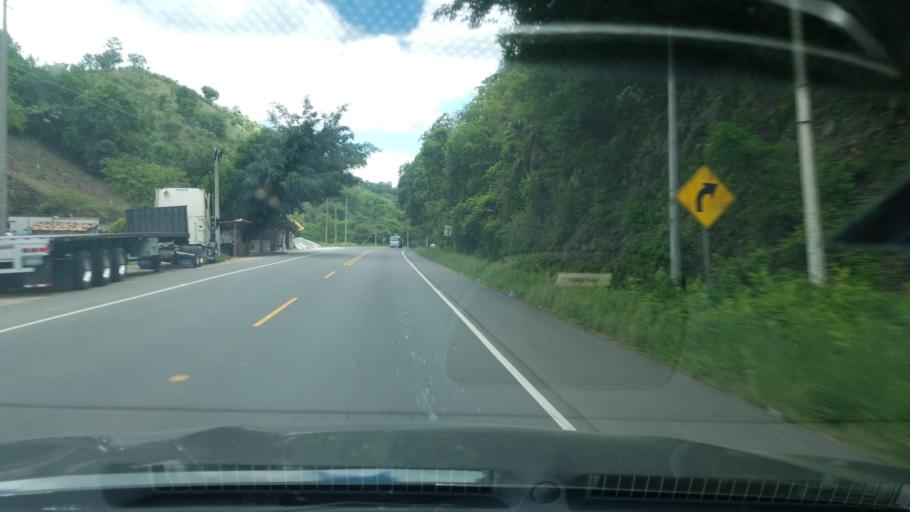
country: HN
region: Francisco Morazan
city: Talanga
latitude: 14.3730
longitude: -87.1367
